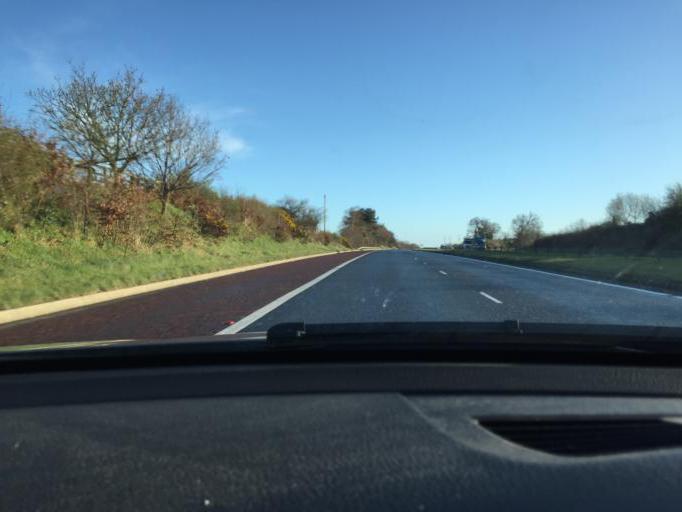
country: GB
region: Northern Ireland
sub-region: Newry and Mourne District
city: Newry
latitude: 54.2579
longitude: -6.3179
